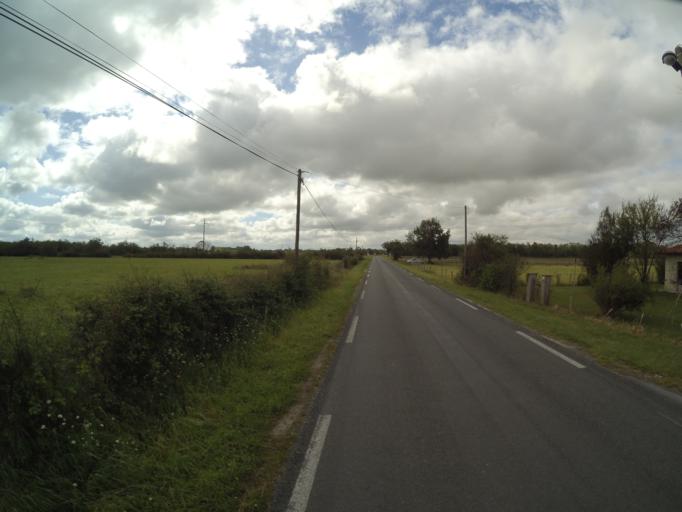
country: FR
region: Aquitaine
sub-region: Departement de la Gironde
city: Ludon-Medoc
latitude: 45.0002
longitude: -0.5988
